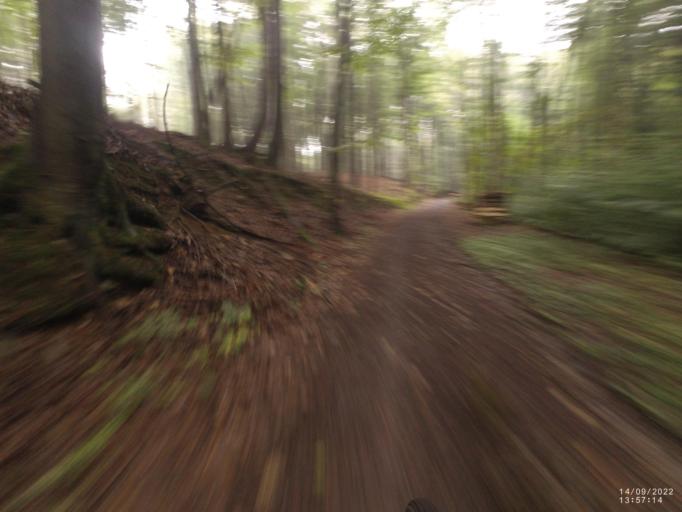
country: DE
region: Bavaria
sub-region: Regierungsbezirk Unterfranken
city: Glattbach
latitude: 50.0142
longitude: 9.1435
